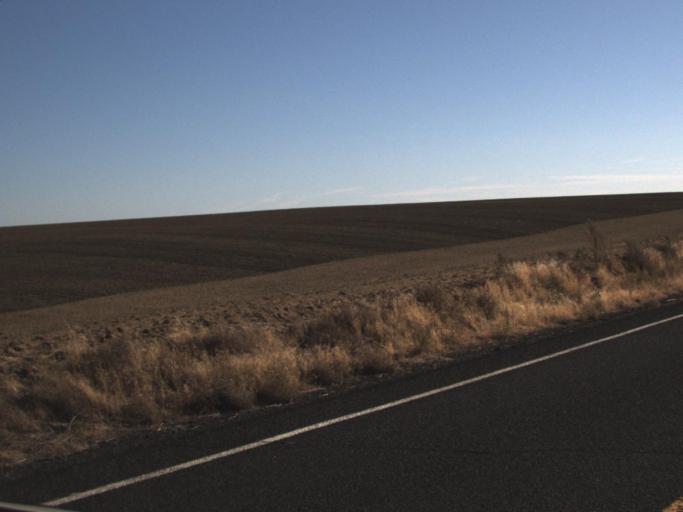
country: US
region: Washington
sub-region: Franklin County
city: Connell
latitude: 46.7315
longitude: -118.5479
